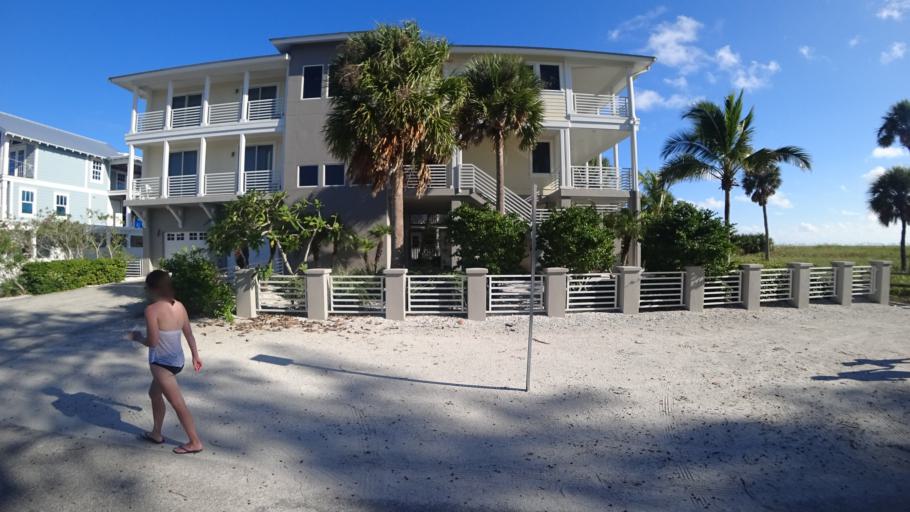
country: US
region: Florida
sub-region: Manatee County
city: Anna Maria
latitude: 27.5229
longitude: -82.7331
